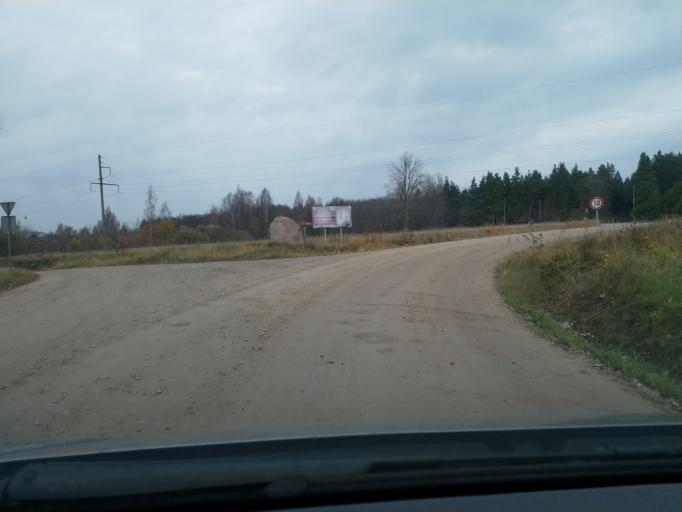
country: LV
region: Kuldigas Rajons
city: Kuldiga
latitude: 56.9827
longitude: 21.9738
